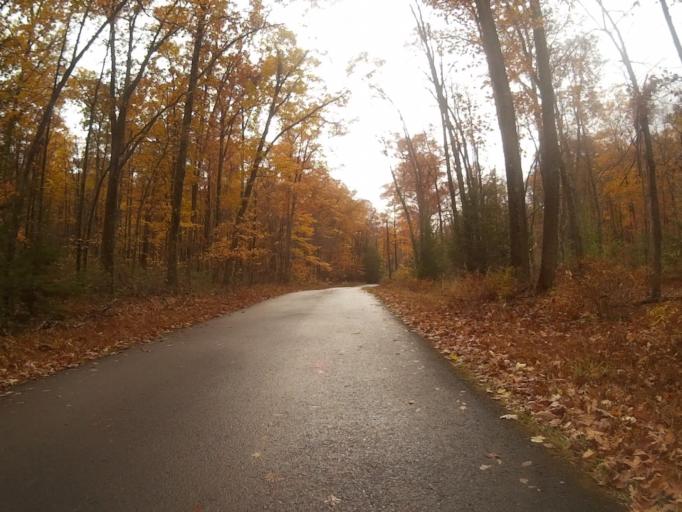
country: US
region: Pennsylvania
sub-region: Centre County
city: Boalsburg
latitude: 40.7500
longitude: -77.7407
